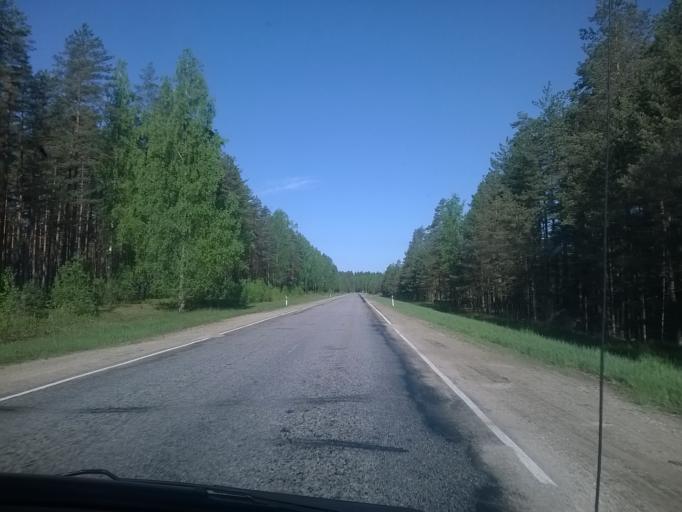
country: LV
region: Strenci
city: Seda
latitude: 57.6248
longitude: 25.7571
